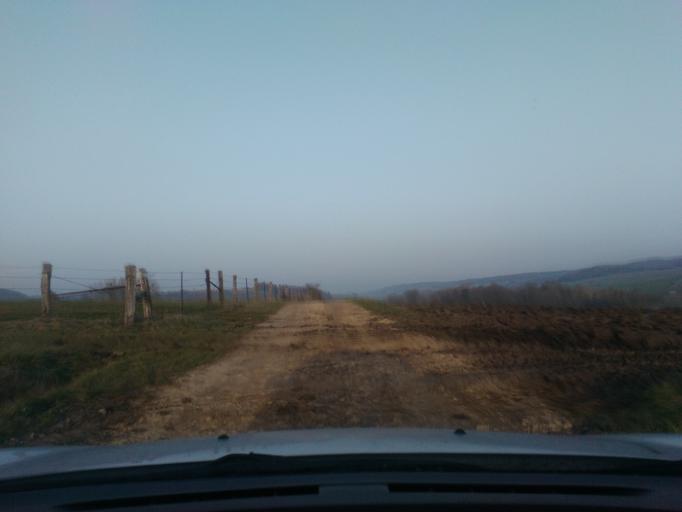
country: FR
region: Lorraine
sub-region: Departement des Vosges
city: Vittel
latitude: 48.2626
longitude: 6.0179
